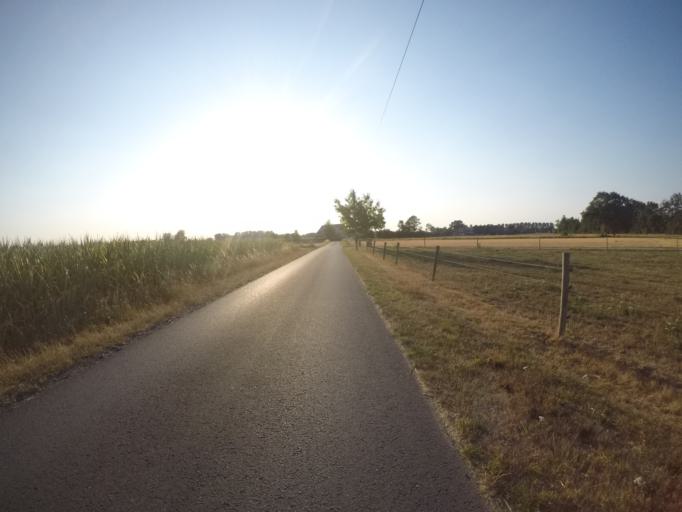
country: NL
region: Gelderland
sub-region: Gemeente Aalten
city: Aalten
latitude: 51.8638
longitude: 6.5385
